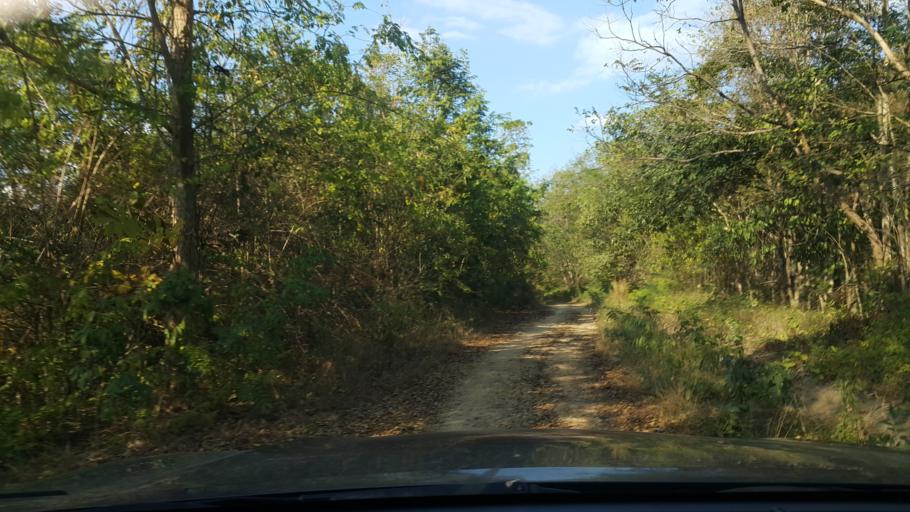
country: TH
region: Sukhothai
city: Thung Saliam
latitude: 17.3326
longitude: 99.4660
